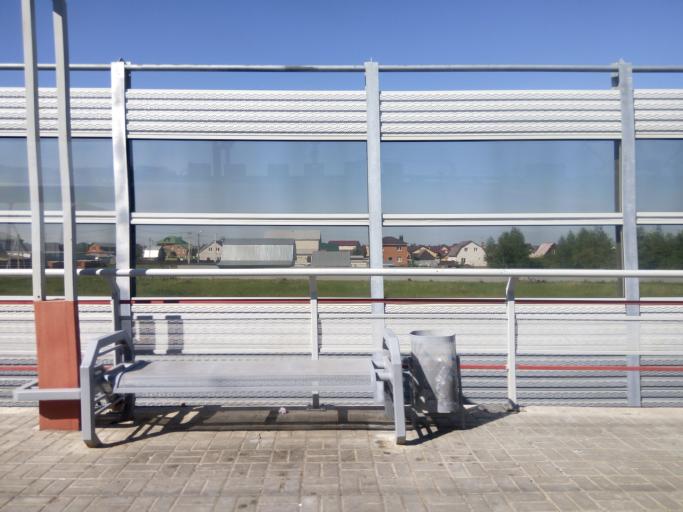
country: RU
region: Tatarstan
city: Stolbishchi
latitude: 55.6525
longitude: 49.2308
